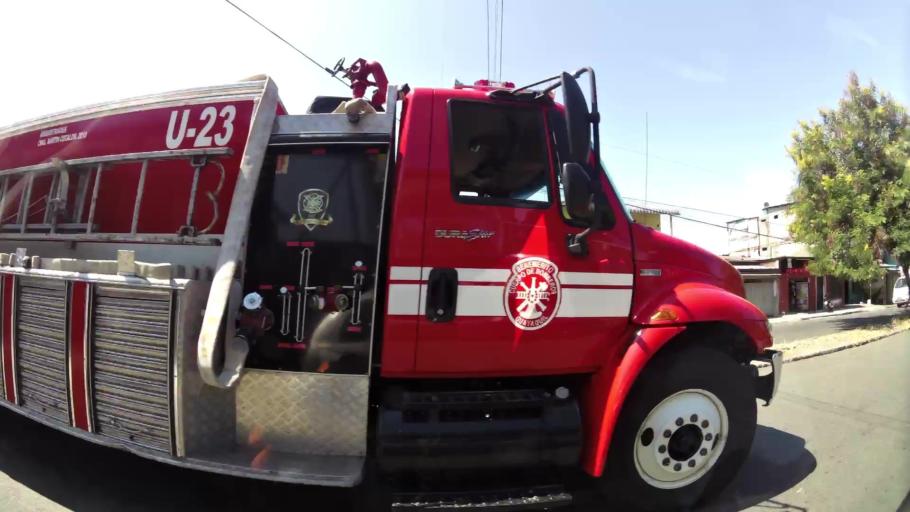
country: EC
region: Guayas
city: Guayaquil
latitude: -2.2268
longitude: -79.9406
